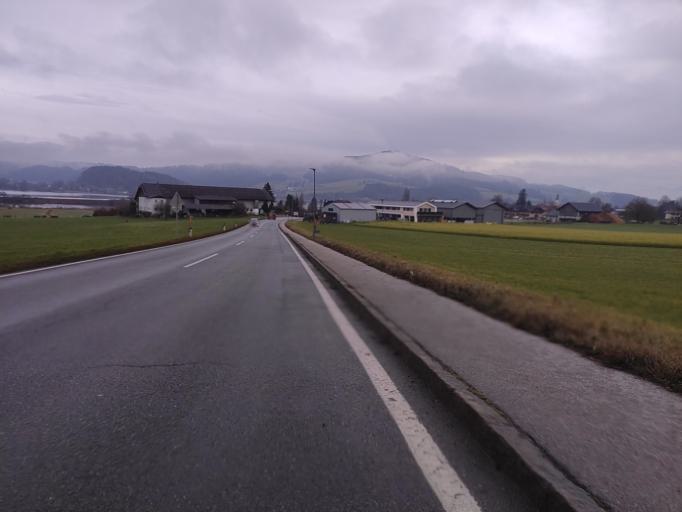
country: AT
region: Salzburg
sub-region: Politischer Bezirk Salzburg-Umgebung
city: Seeham
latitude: 47.9740
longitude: 13.0741
